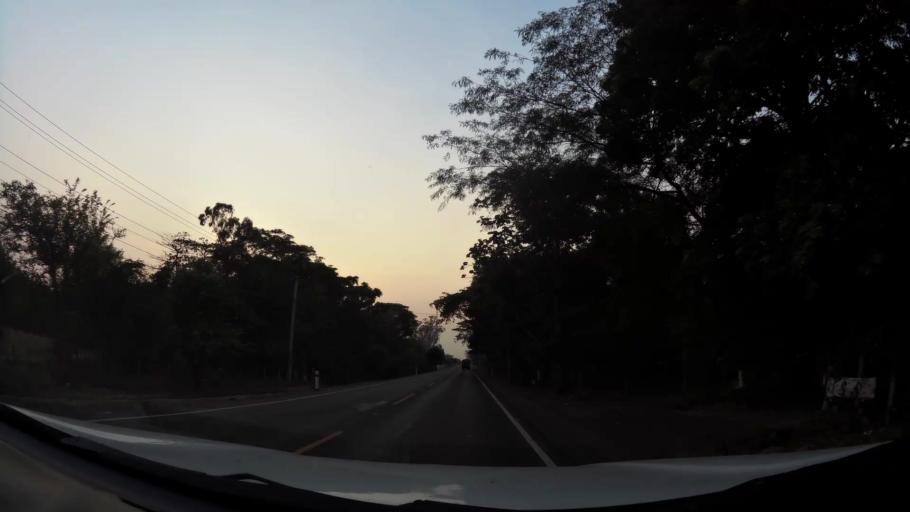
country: NI
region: Leon
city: Leon
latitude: 12.3346
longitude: -86.8101
